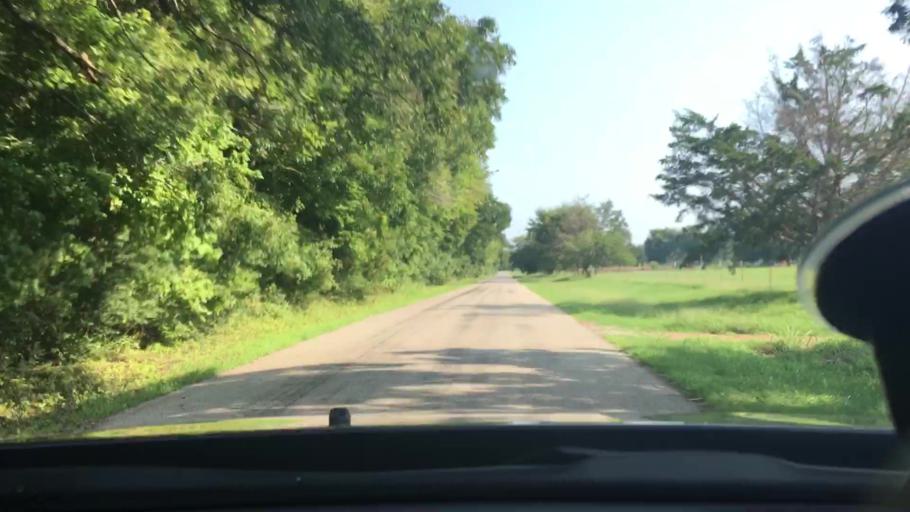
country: US
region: Oklahoma
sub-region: Johnston County
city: Tishomingo
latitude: 34.2087
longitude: -96.6691
